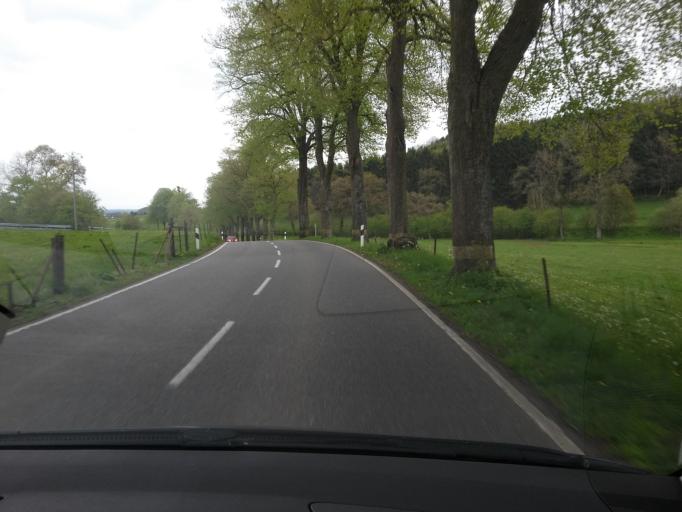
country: LU
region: Luxembourg
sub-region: Canton de Capellen
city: Garnich
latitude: 49.6080
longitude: 5.9376
